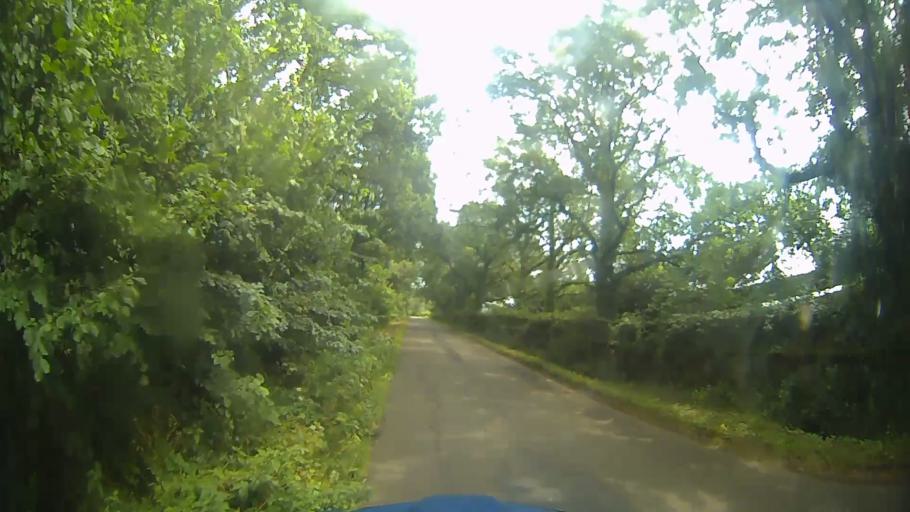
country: GB
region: England
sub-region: Hampshire
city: Lindford
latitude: 51.1505
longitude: -0.8394
